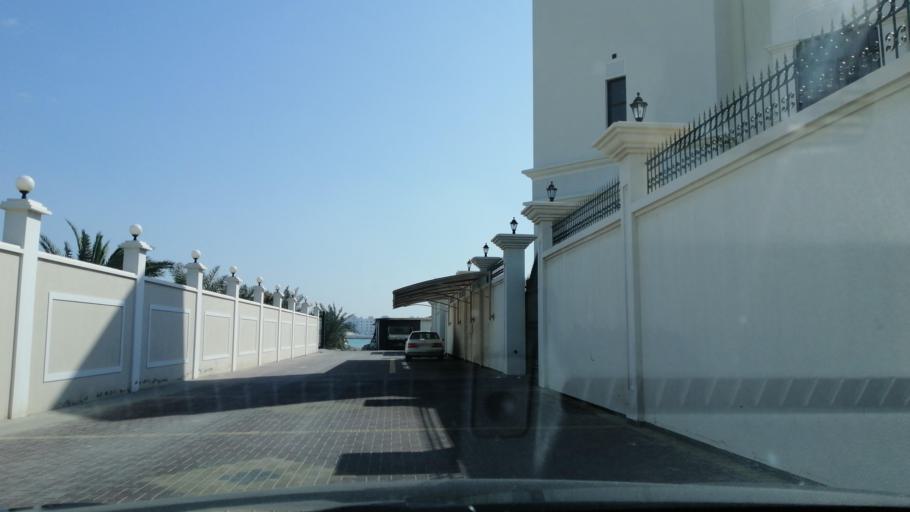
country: BH
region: Muharraq
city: Al Hadd
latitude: 26.2402
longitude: 50.6361
